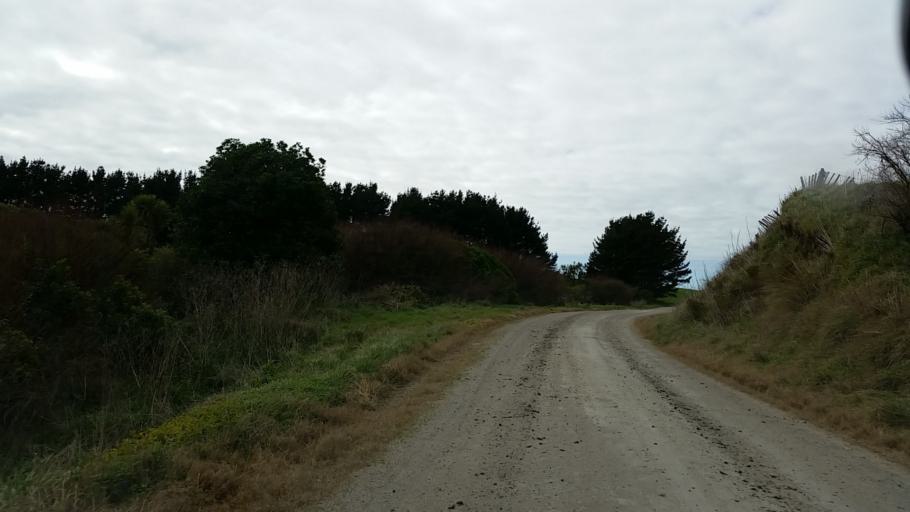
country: NZ
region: Taranaki
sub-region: South Taranaki District
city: Patea
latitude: -39.8017
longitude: 174.6824
